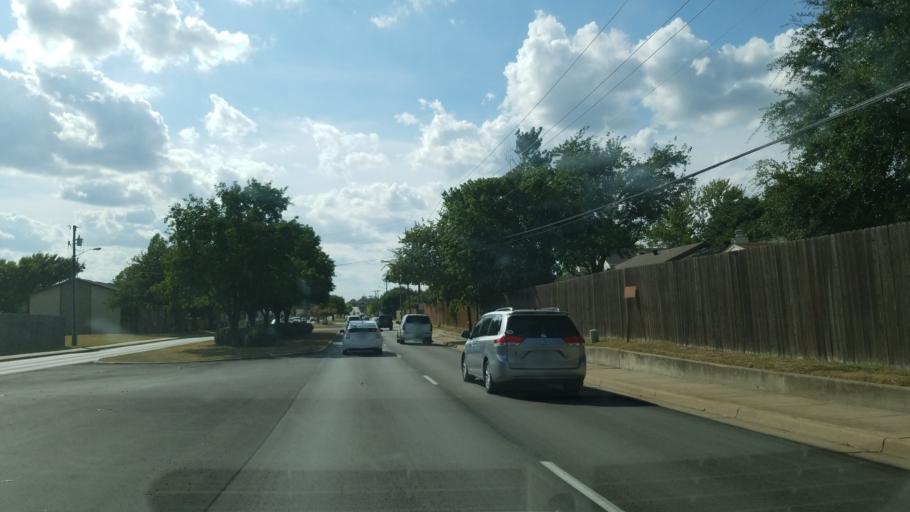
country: US
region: Texas
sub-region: Tarrant County
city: Bedford
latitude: 32.8521
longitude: -97.1261
